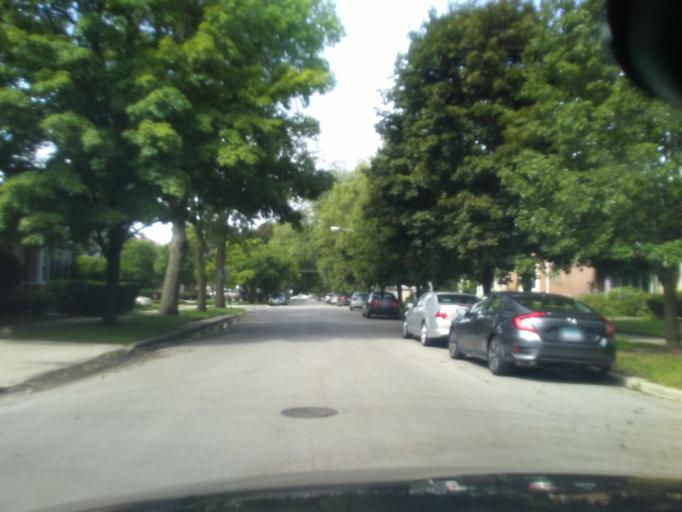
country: US
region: Illinois
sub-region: Cook County
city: Evanston
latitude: 42.0167
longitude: -87.6978
